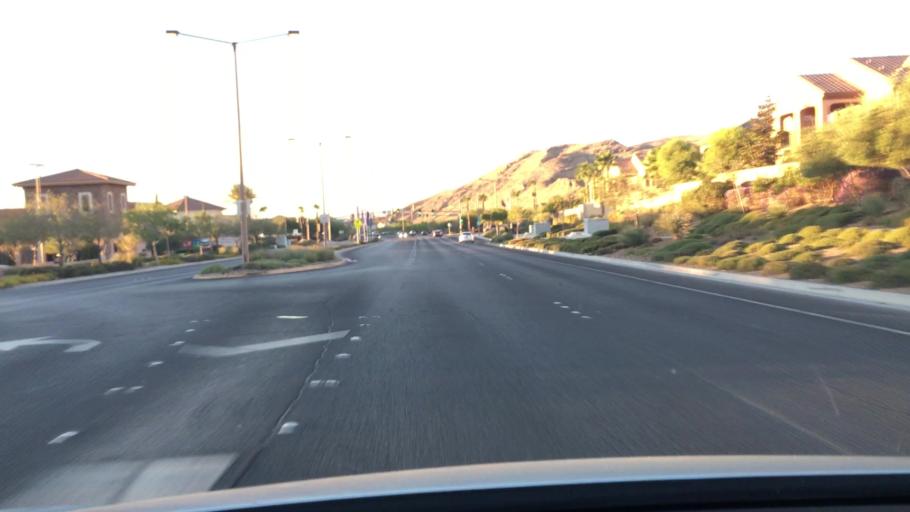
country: US
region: Nevada
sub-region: Clark County
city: Summerlin South
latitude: 36.1609
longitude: -115.3523
